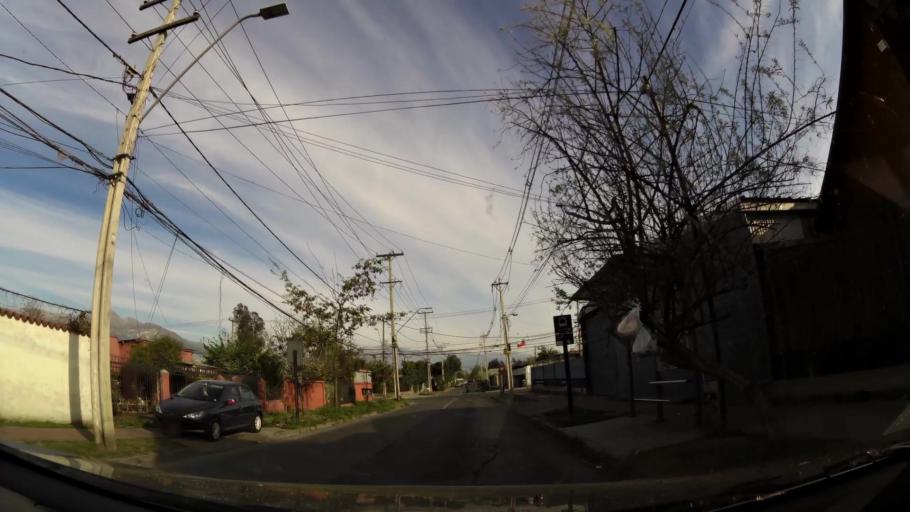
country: CL
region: Santiago Metropolitan
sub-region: Provincia de Cordillera
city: Puente Alto
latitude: -33.6151
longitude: -70.5694
